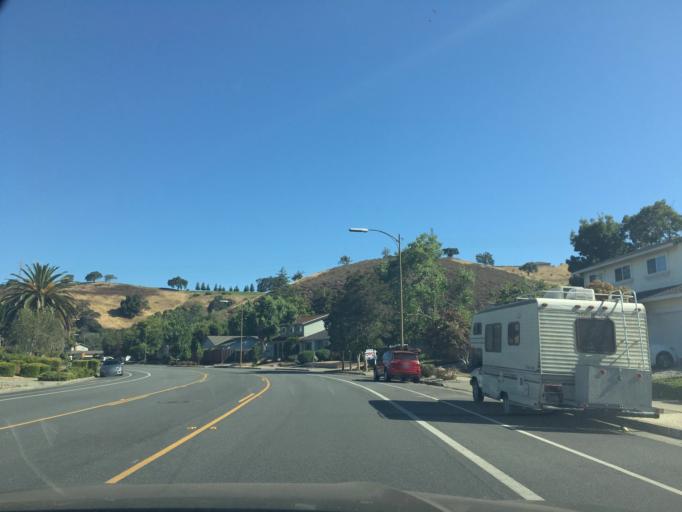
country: US
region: California
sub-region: Santa Clara County
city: Seven Trees
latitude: 37.2260
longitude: -121.8600
